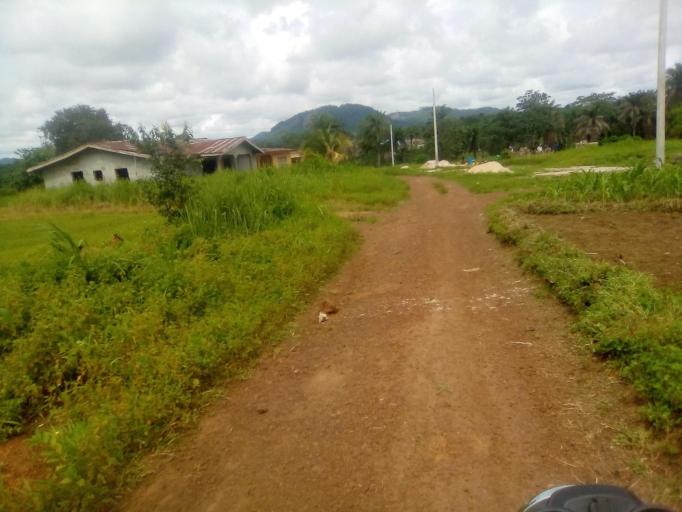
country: SL
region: Southern Province
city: Moyamba
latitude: 8.1472
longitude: -12.4338
